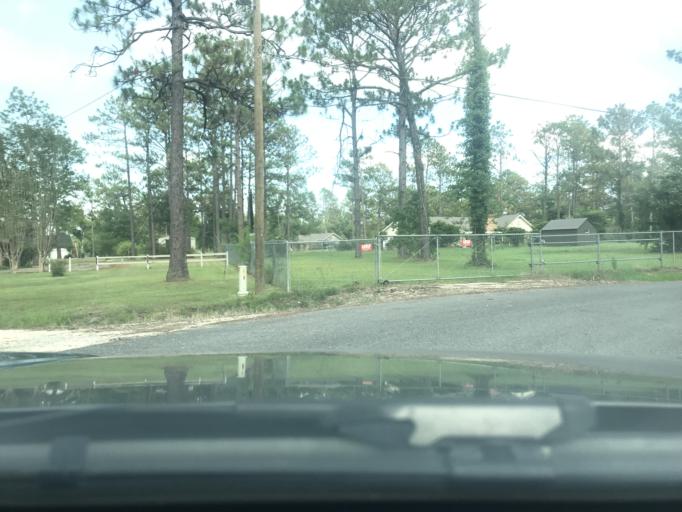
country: US
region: Louisiana
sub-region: Calcasieu Parish
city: Moss Bluff
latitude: 30.3390
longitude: -93.2626
